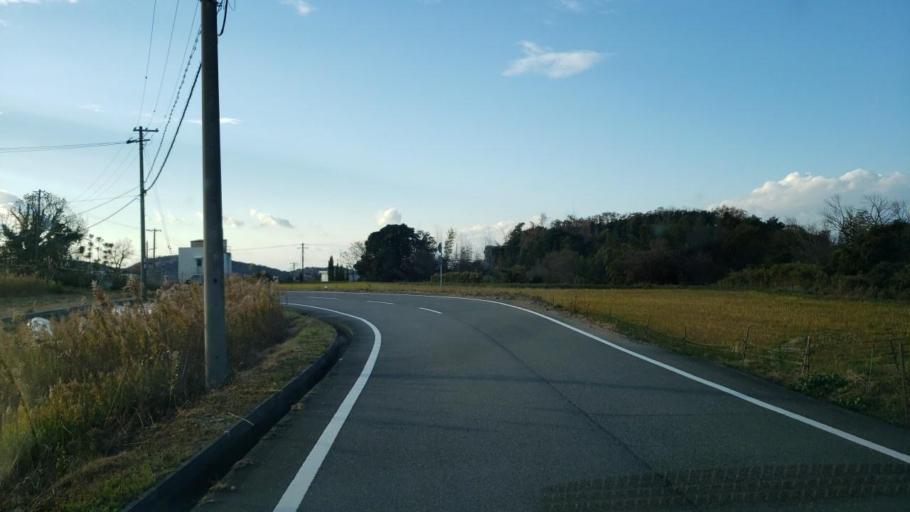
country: JP
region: Hyogo
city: Akashi
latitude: 34.5449
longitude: 134.9705
